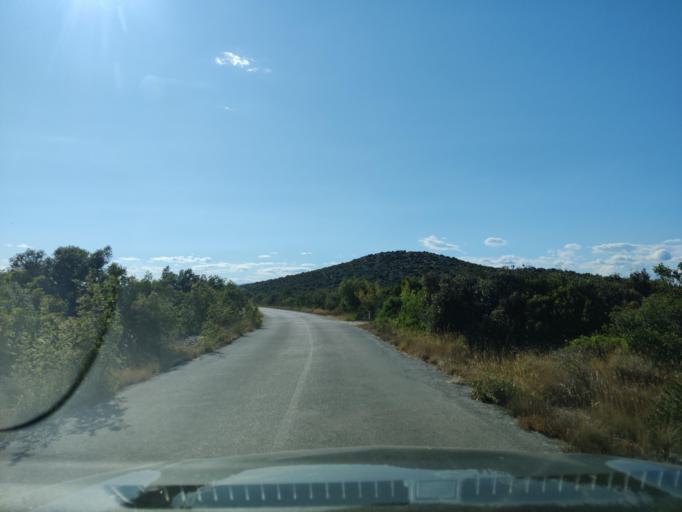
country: HR
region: Sibensko-Kniniska
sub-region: Grad Sibenik
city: Sibenik
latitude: 43.7390
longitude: 15.8707
